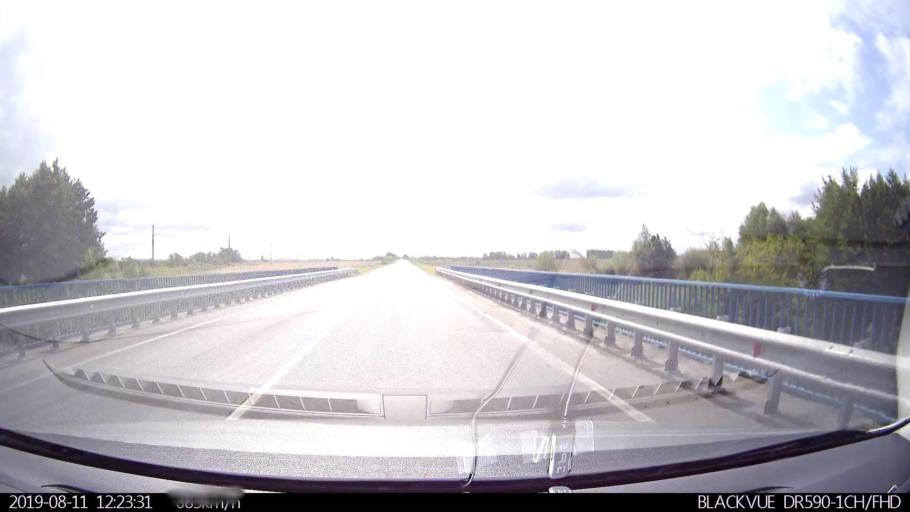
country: RU
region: Ulyanovsk
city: Ignatovka
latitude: 53.8942
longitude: 47.9503
